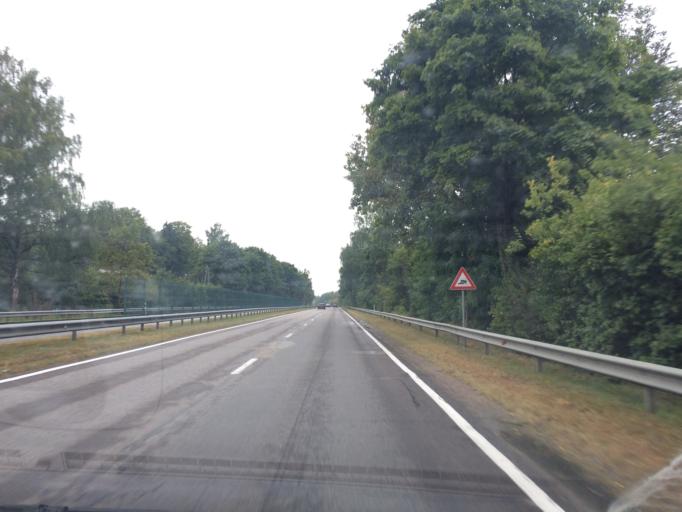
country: LV
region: Ikskile
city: Ikskile
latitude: 56.8389
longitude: 24.4919
